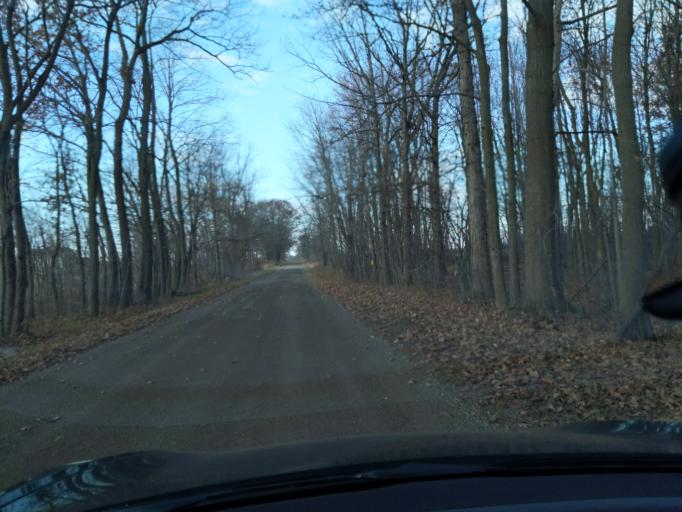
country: US
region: Michigan
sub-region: Ingham County
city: Williamston
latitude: 42.7212
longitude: -84.3253
